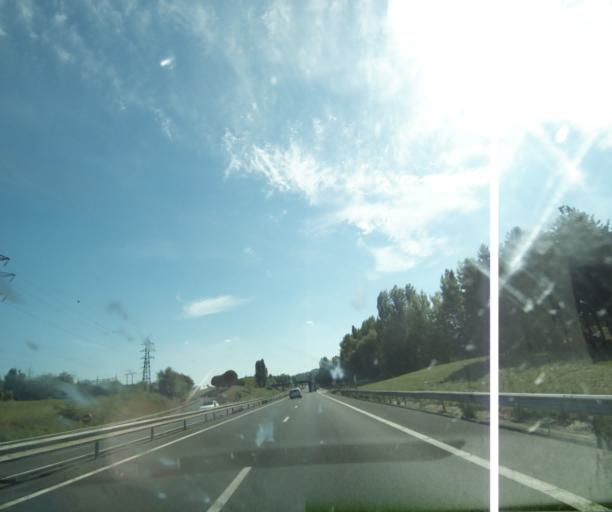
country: FR
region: Limousin
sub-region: Departement de la Correze
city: Saint-Pantaleon-de-Larche
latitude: 45.1501
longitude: 1.4844
